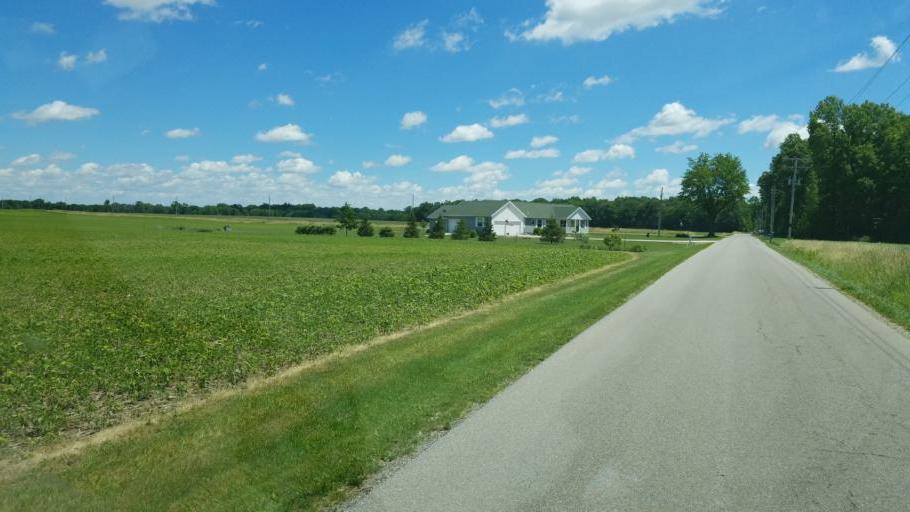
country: US
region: Ohio
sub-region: Crawford County
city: Galion
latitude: 40.7418
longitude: -82.8834
